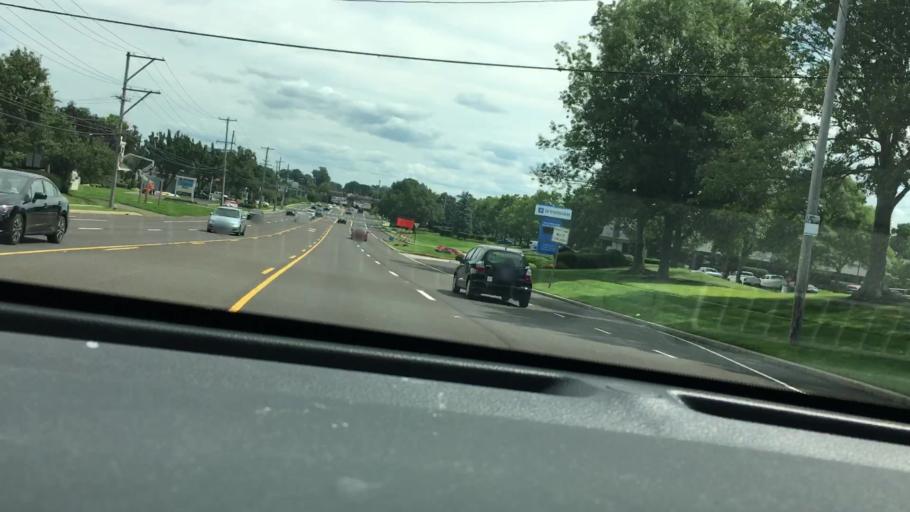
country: US
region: Pennsylvania
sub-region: Bucks County
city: Trevose
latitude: 40.1366
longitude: -74.9830
